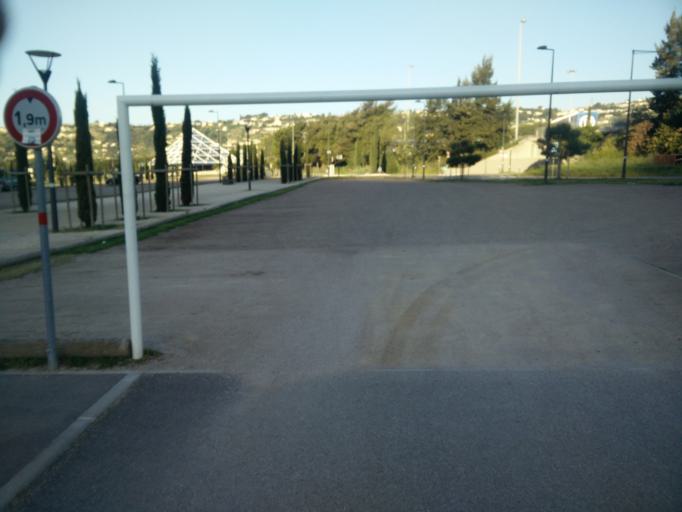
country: FR
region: Provence-Alpes-Cote d'Azur
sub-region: Departement des Alpes-Maritimes
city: Saint-Laurent-du-Var
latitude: 43.7078
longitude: 7.1937
